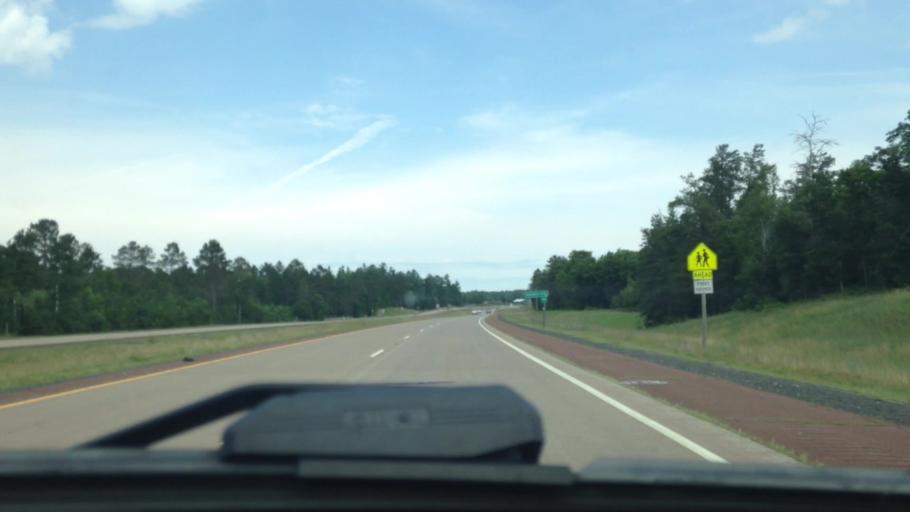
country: US
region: Wisconsin
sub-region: Douglas County
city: Lake Nebagamon
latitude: 46.3420
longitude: -91.8335
